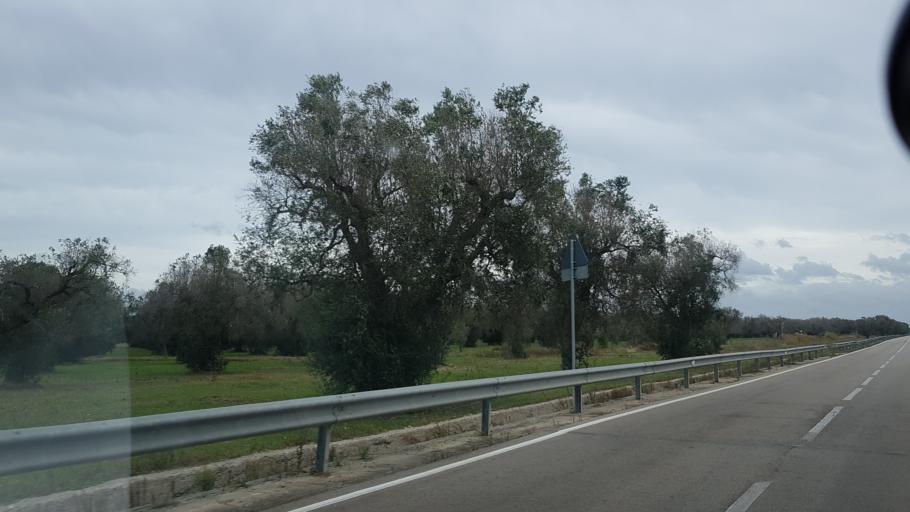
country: IT
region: Apulia
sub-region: Provincia di Brindisi
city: San Pancrazio Salentino
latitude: 40.4078
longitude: 17.8826
